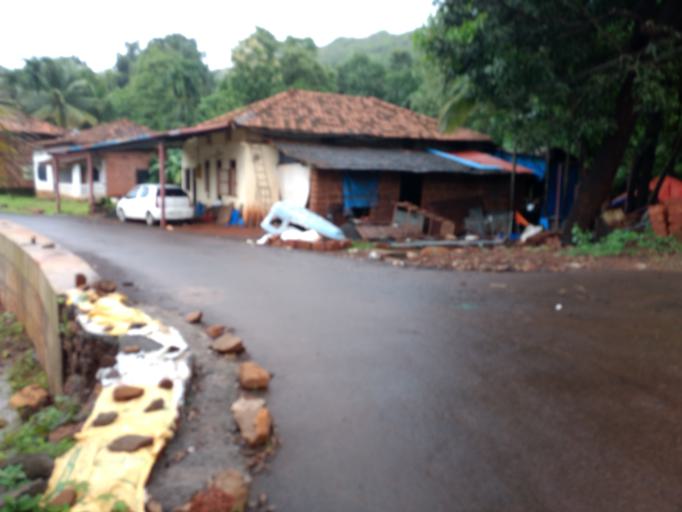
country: IN
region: Maharashtra
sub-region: Ratnagiri
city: Guhagar
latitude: 17.4934
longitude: 73.1899
